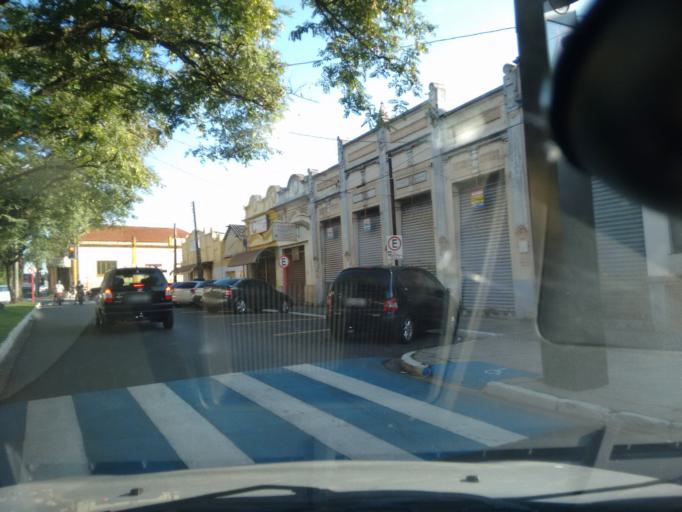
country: BR
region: Sao Paulo
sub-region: Araraquara
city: Araraquara
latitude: -21.7936
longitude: -48.1716
